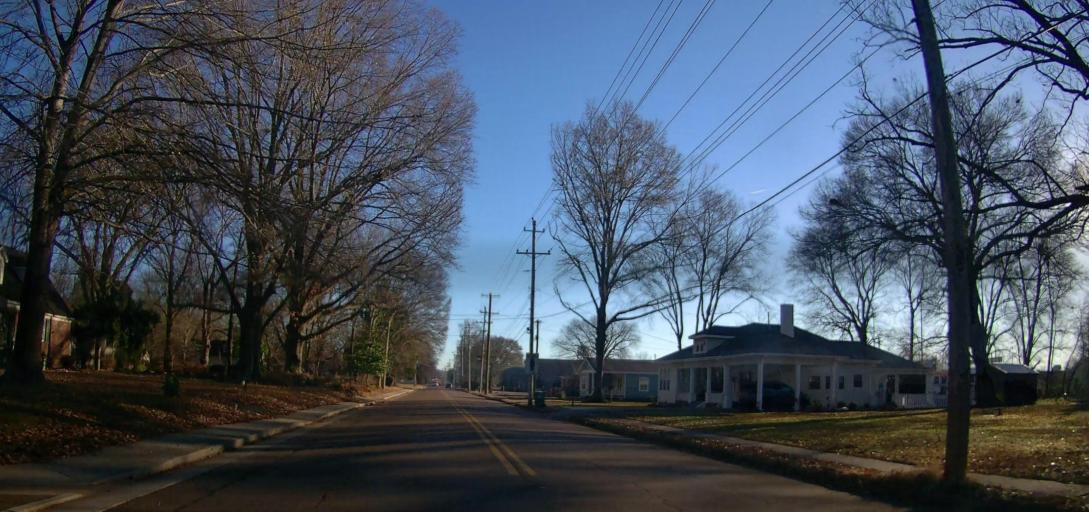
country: US
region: Tennessee
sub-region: Shelby County
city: Millington
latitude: 35.3492
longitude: -89.8956
